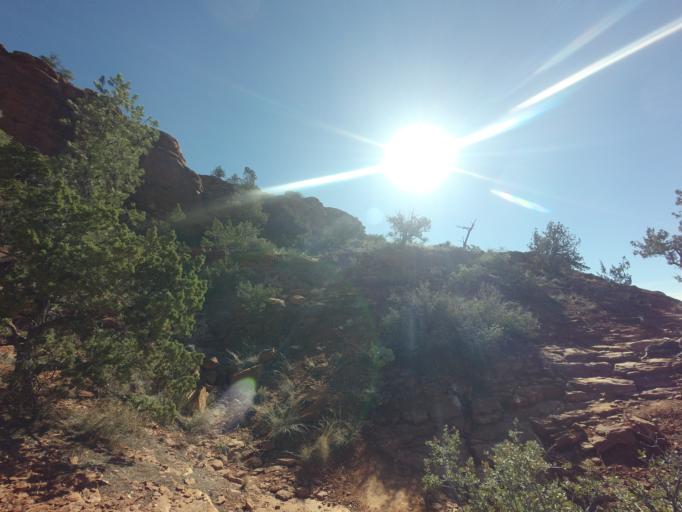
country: US
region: Arizona
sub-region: Yavapai County
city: West Sedona
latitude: 34.8146
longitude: -111.8059
